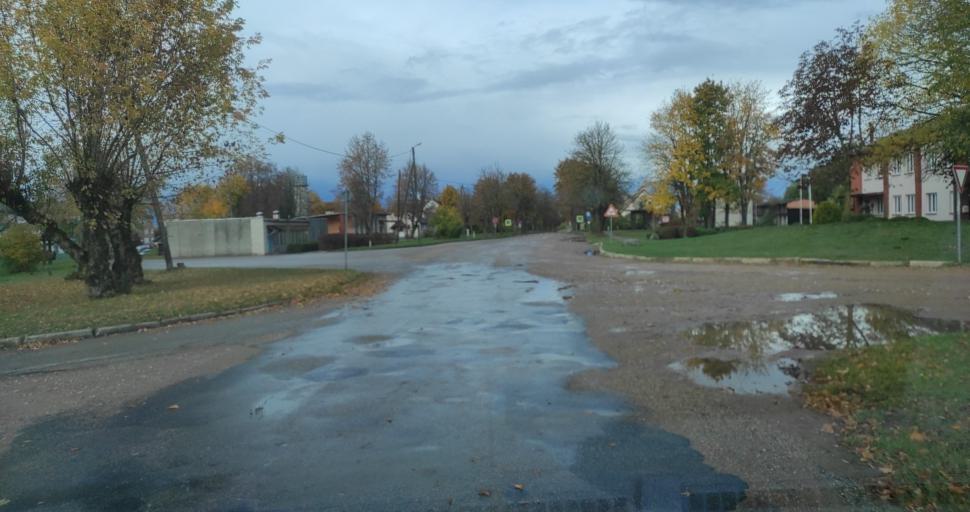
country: LV
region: Vainode
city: Vainode
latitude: 56.5688
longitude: 21.9012
